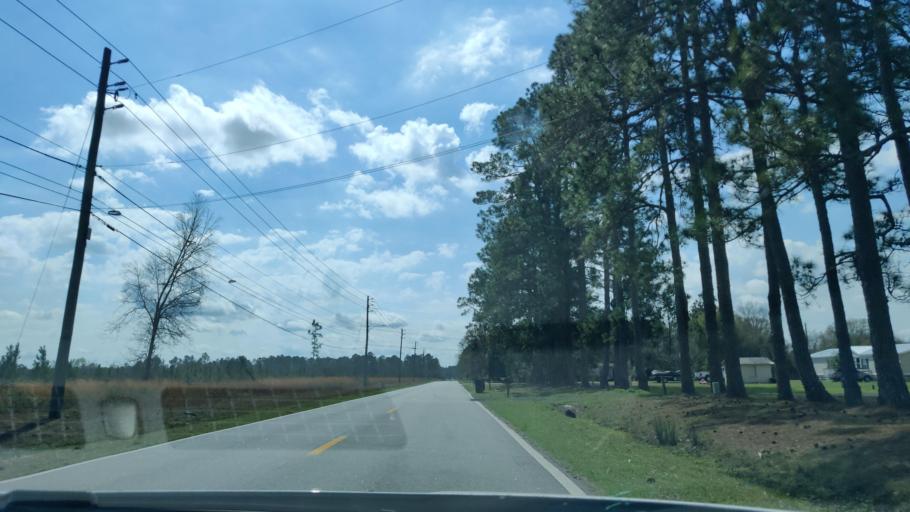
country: US
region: Florida
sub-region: Duval County
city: Baldwin
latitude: 30.2300
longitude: -81.9411
